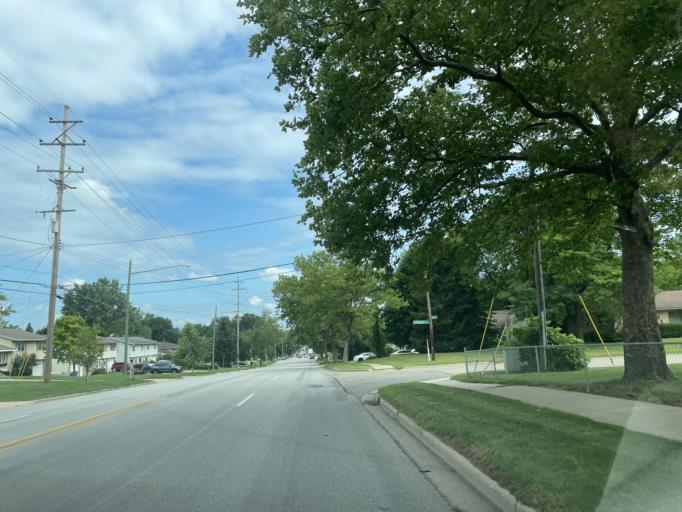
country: US
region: Michigan
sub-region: Kent County
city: Kentwood
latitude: 42.8957
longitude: -85.6265
